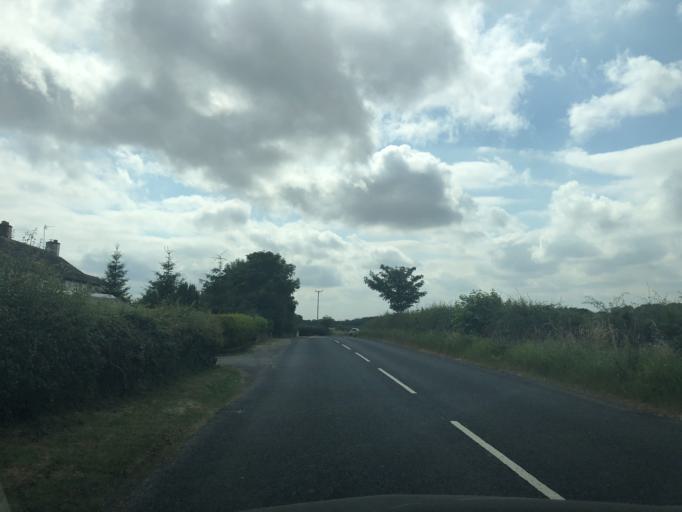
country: GB
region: England
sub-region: North Yorkshire
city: Stokesley
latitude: 54.4589
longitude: -1.2433
